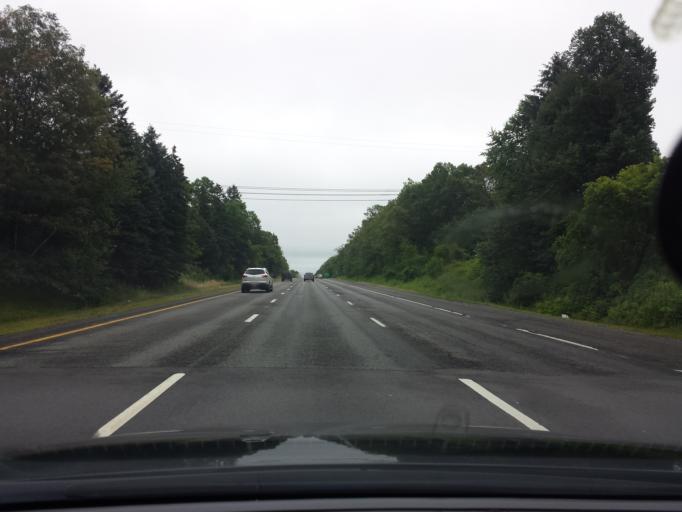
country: US
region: Massachusetts
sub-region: Bristol County
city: Seekonk
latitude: 41.7995
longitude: -71.3253
